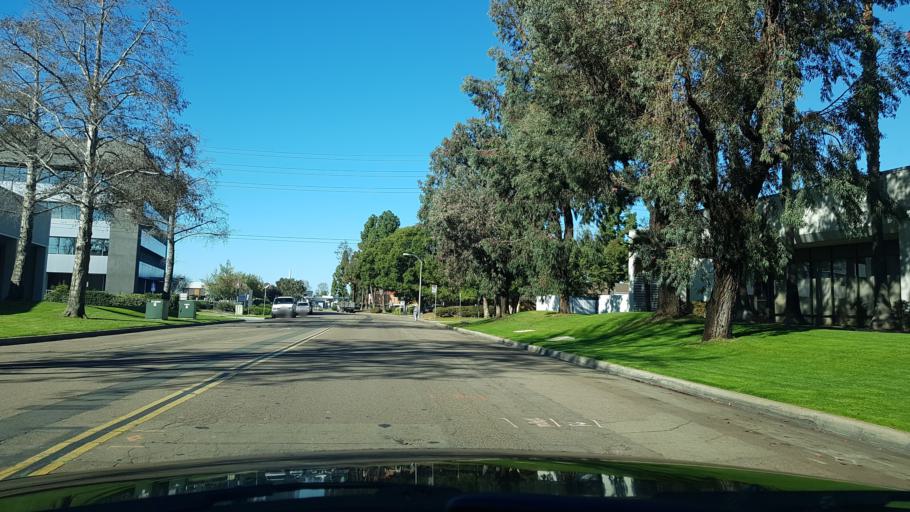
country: US
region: California
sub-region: San Diego County
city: San Diego
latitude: 32.8300
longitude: -117.1373
